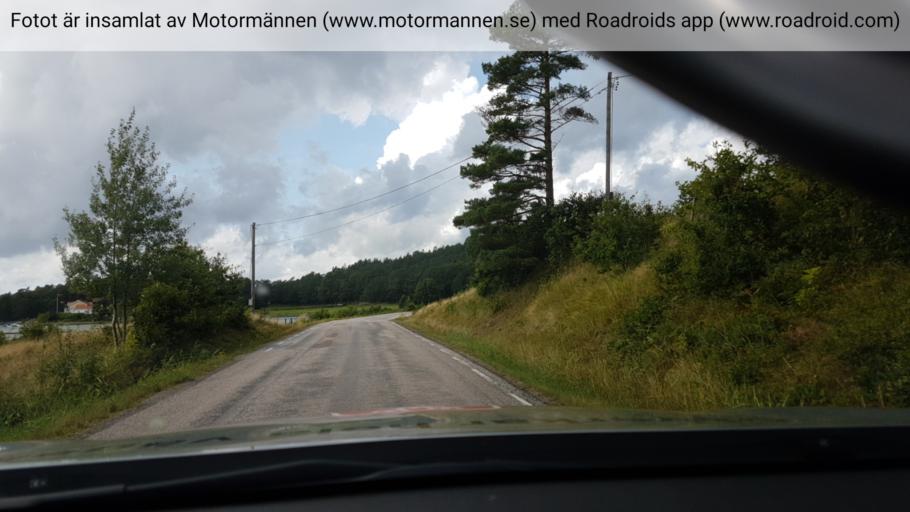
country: SE
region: Vaestra Goetaland
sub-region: Uddevalla Kommun
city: Ljungskile
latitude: 58.2580
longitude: 11.8553
